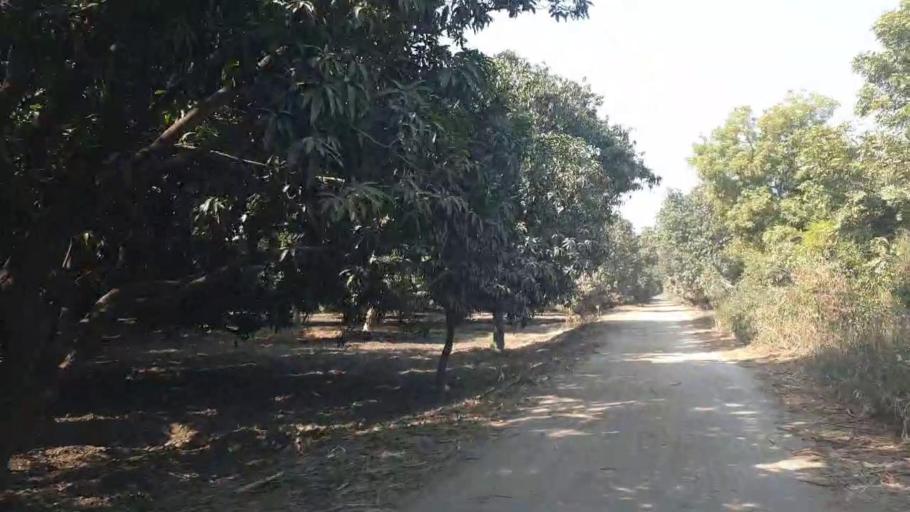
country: PK
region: Sindh
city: Tando Allahyar
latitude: 25.4663
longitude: 68.7753
